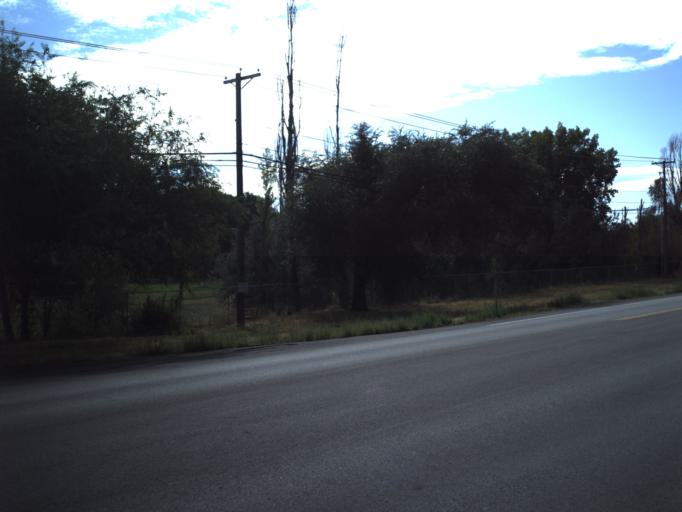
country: US
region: Utah
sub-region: Salt Lake County
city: Salt Lake City
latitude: 40.7948
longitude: -111.9393
